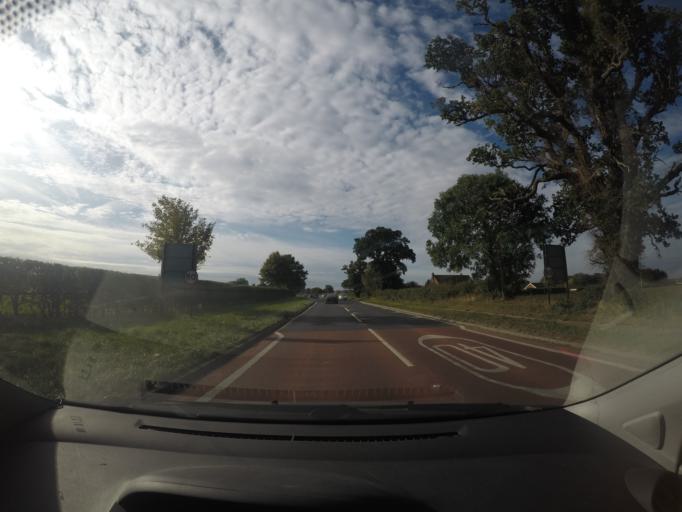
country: GB
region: England
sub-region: City of York
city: Deighton
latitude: 53.8877
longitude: -1.0461
